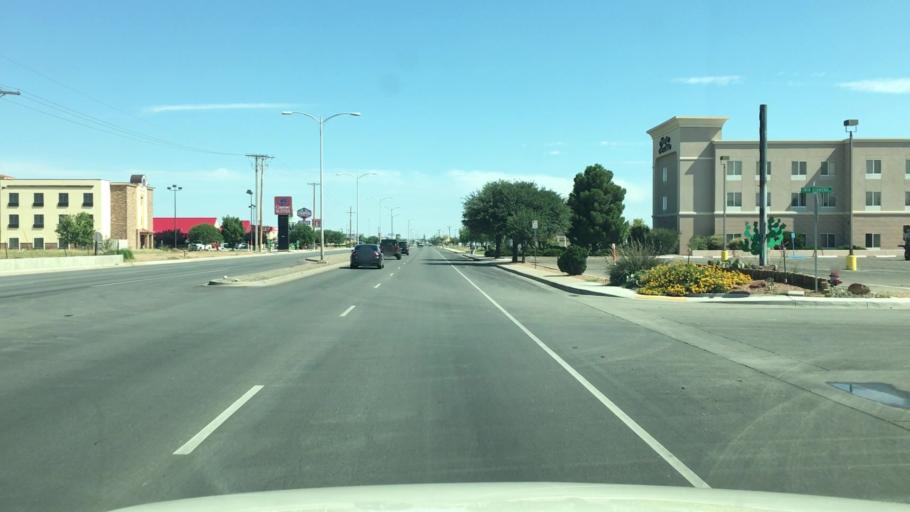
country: US
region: New Mexico
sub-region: Chaves County
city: Roswell
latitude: 33.4409
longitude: -104.5231
